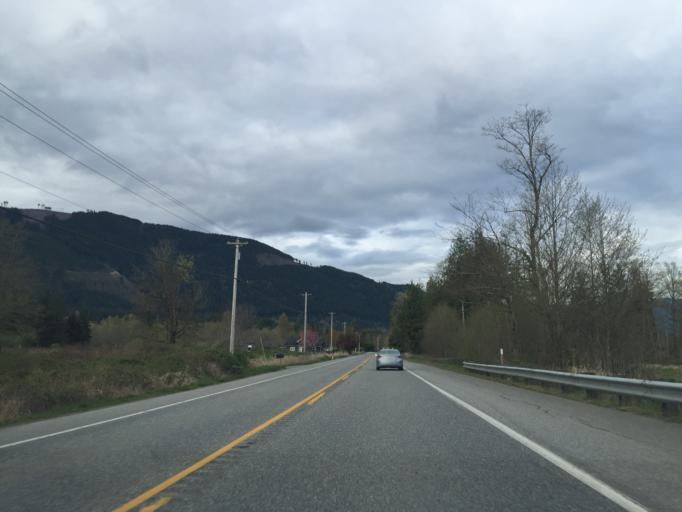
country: US
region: Washington
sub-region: Snohomish County
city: Arlington Heights
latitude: 48.2707
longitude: -122.0035
